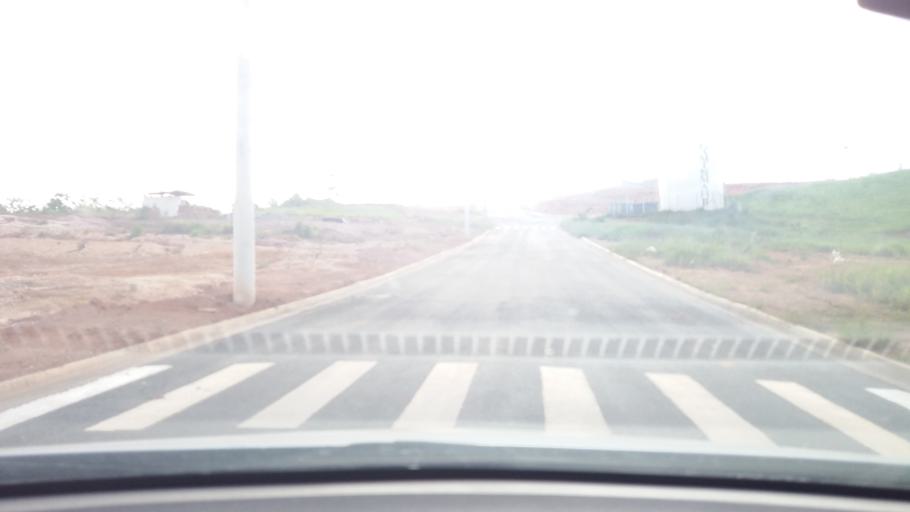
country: BR
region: Sao Paulo
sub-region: Bom Jesus Dos Perdoes
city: Bom Jesus dos Perdoes
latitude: -23.1544
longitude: -46.4729
